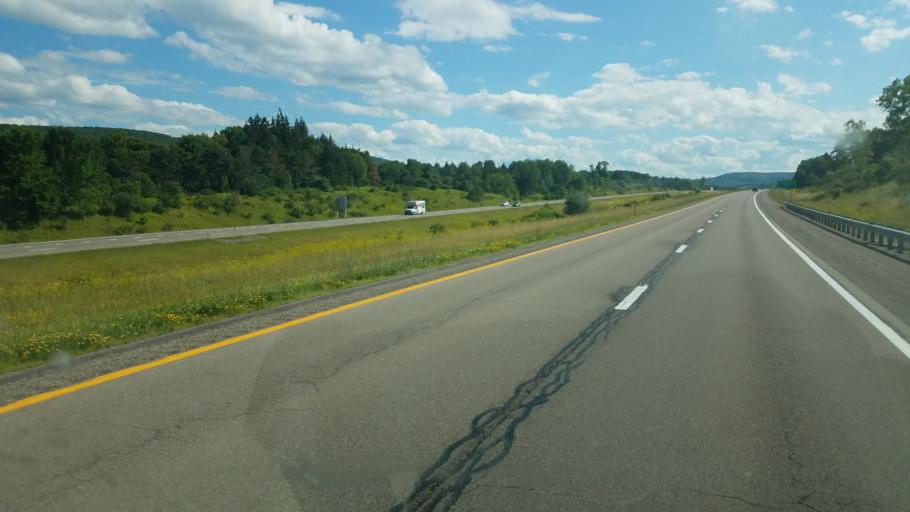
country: US
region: New York
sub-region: Steuben County
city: Hornell
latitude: 42.3391
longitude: -77.7292
